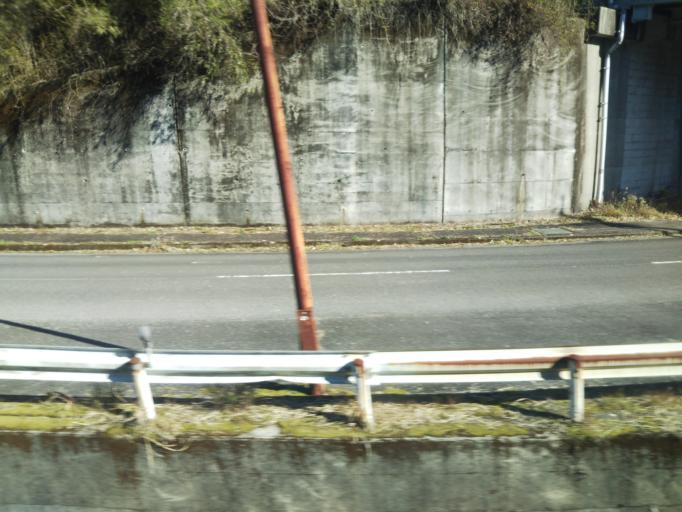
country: JP
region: Kochi
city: Nakamura
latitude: 33.1028
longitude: 133.0986
